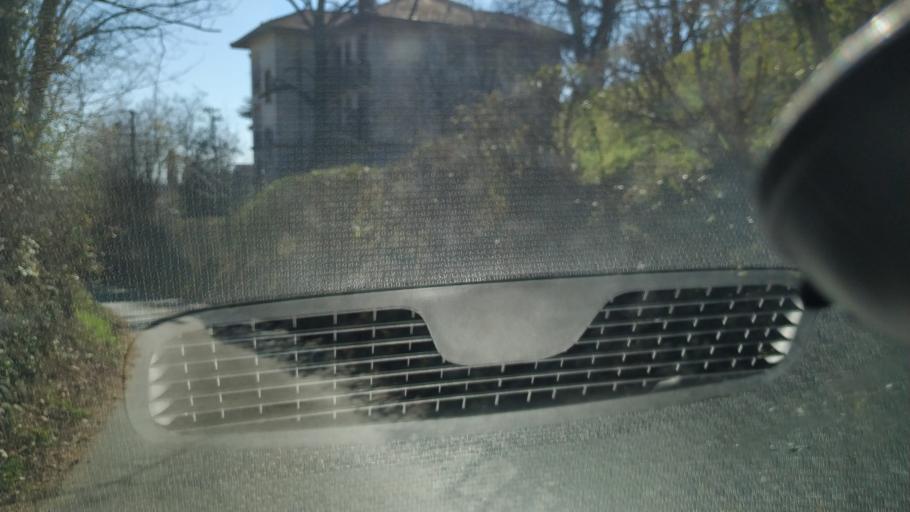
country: IT
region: Piedmont
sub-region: Provincia di Vercelli
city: Gattinara
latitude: 45.6202
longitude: 8.3654
